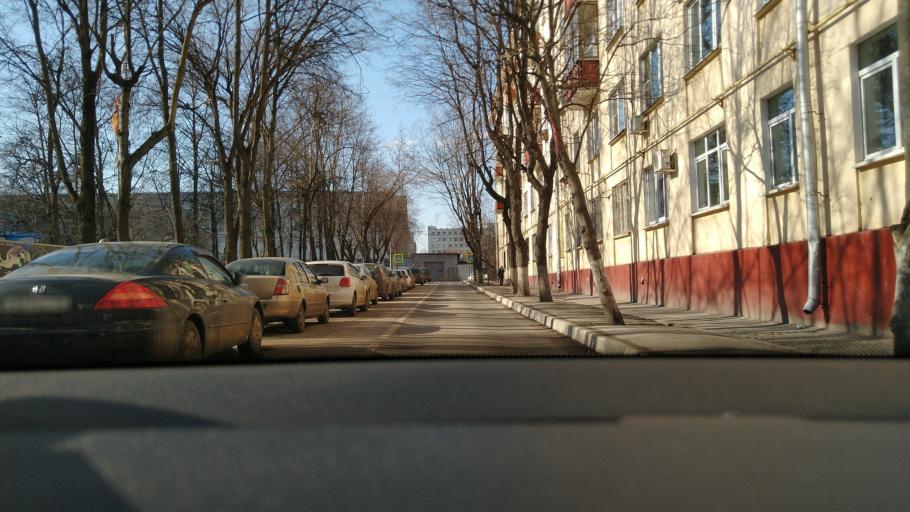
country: RU
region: Moscow
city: Khimki
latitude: 55.9013
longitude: 37.4526
